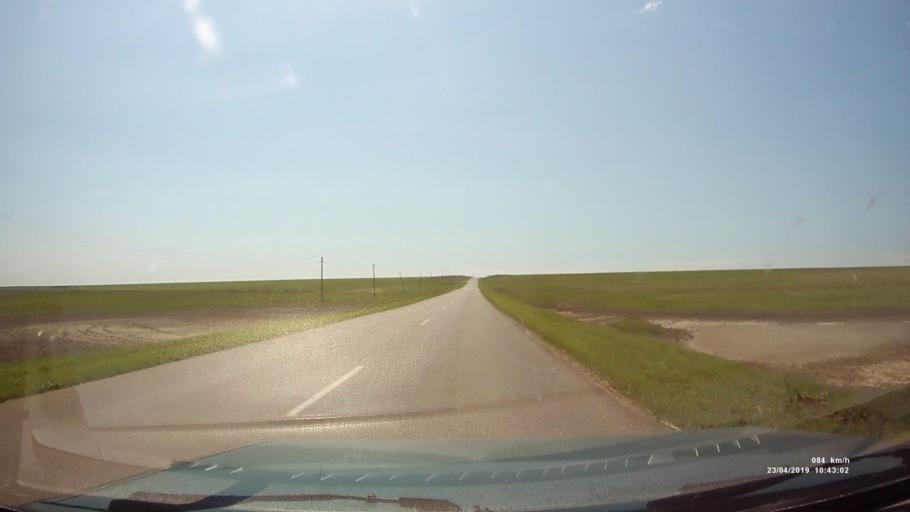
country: RU
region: Kalmykiya
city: Yashalta
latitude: 46.4750
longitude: 42.6481
